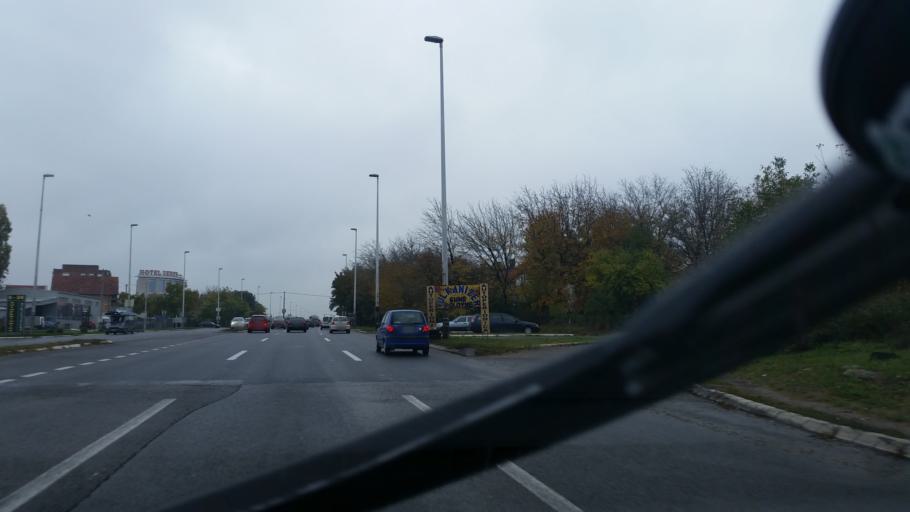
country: RS
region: Central Serbia
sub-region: Belgrade
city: Zemun
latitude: 44.8390
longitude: 20.3661
